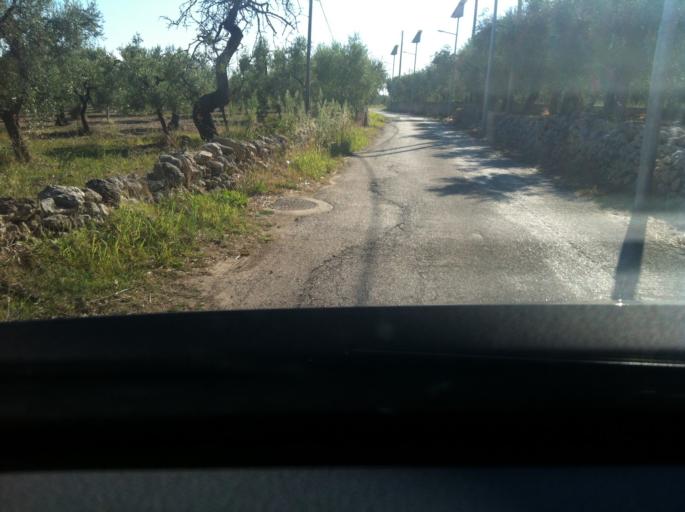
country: IT
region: Apulia
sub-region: Provincia di Foggia
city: Monte Sant'Angelo
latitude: 41.6569
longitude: 15.9712
